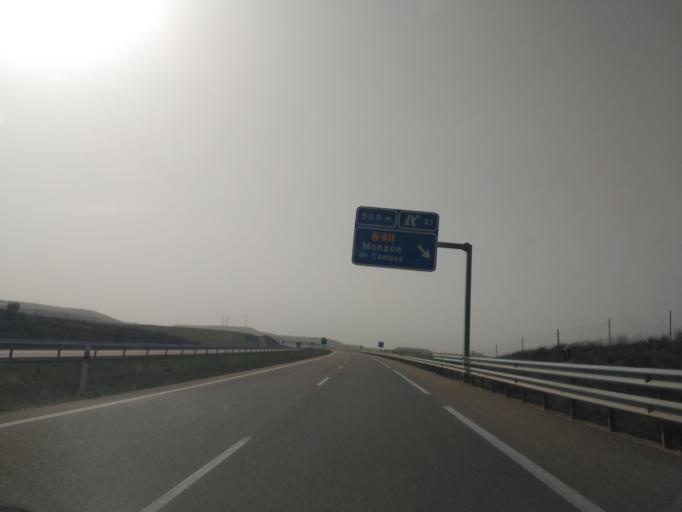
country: ES
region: Castille and Leon
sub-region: Provincia de Palencia
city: Monzon de Campos
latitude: 42.1283
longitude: -4.4771
